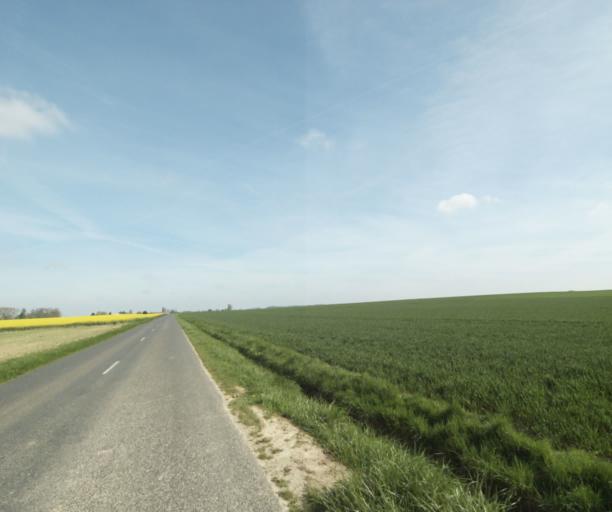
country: FR
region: Ile-de-France
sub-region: Departement de Seine-et-Marne
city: Nangis
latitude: 48.5716
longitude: 3.0123
